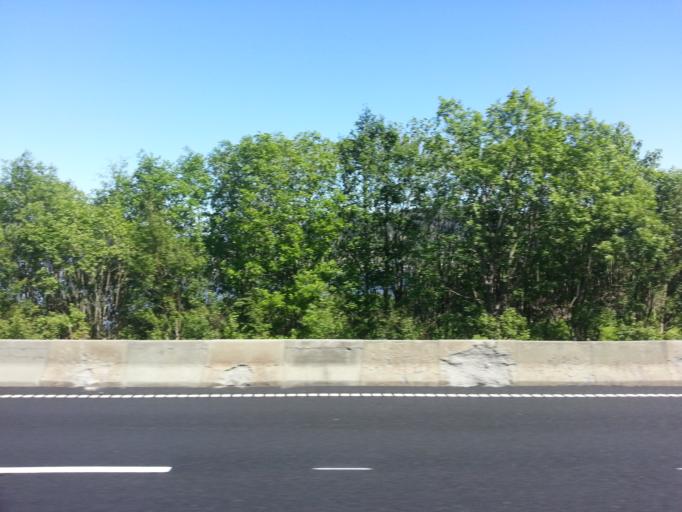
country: NO
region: Sor-Trondelag
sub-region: Malvik
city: Hommelvik
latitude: 63.4131
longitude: 10.7697
